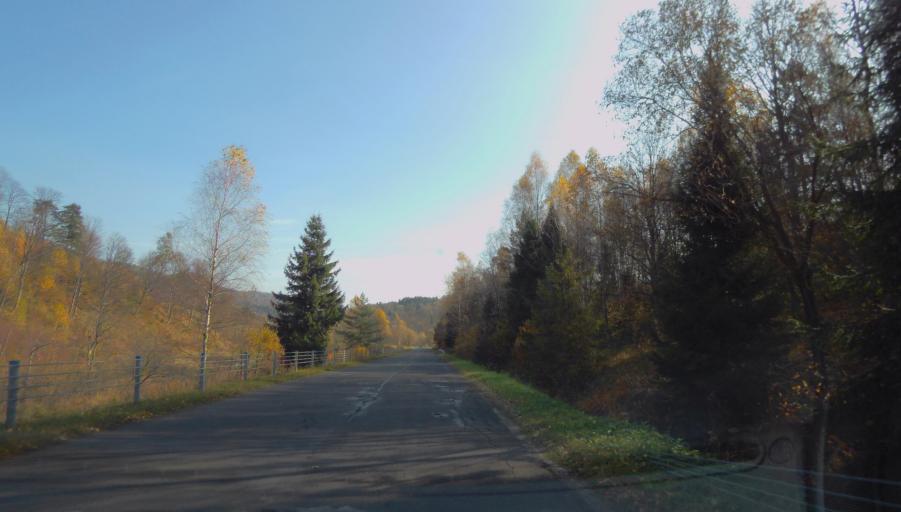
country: PL
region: Subcarpathian Voivodeship
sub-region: Powiat leski
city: Cisna
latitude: 49.2070
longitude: 22.2531
